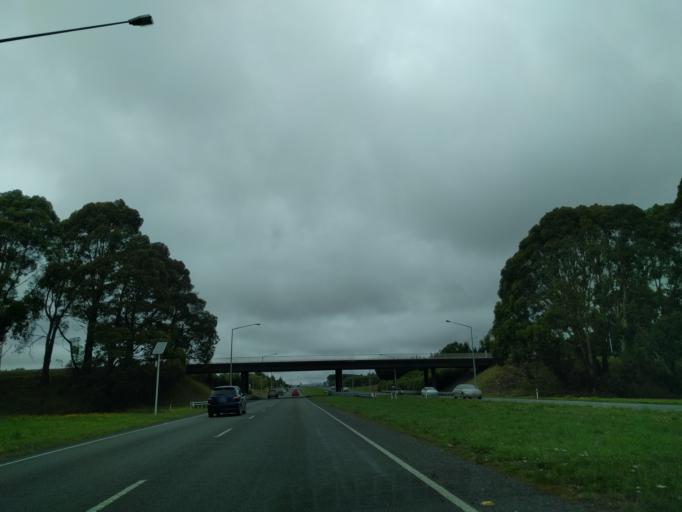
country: NZ
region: Canterbury
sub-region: Waimakariri District
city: Kaiapoi
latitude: -43.4069
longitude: 172.6444
